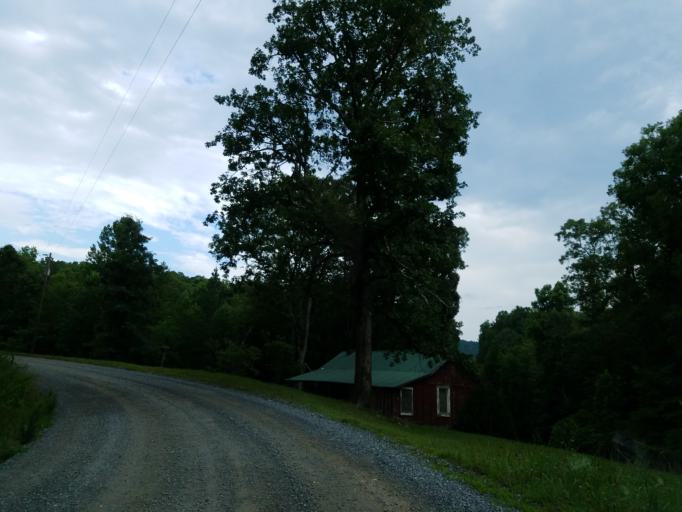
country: US
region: Georgia
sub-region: Fannin County
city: Blue Ridge
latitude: 34.8307
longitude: -84.2313
